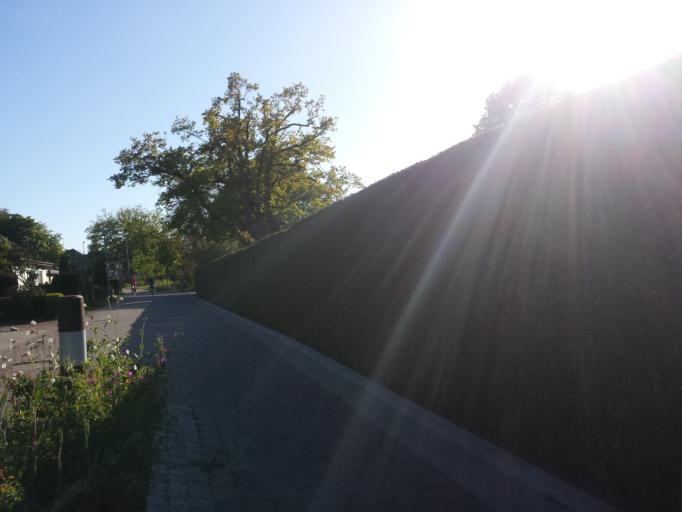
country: DE
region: Lower Saxony
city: Lilienthal
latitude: 53.1542
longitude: 8.9334
